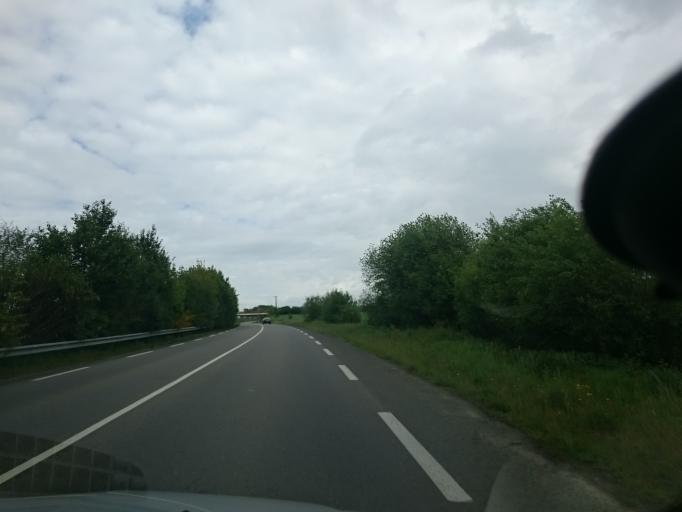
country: FR
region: Brittany
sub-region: Departement d'Ille-et-Vilaine
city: Saint-Etienne-en-Cogles
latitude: 48.3946
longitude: -1.3222
